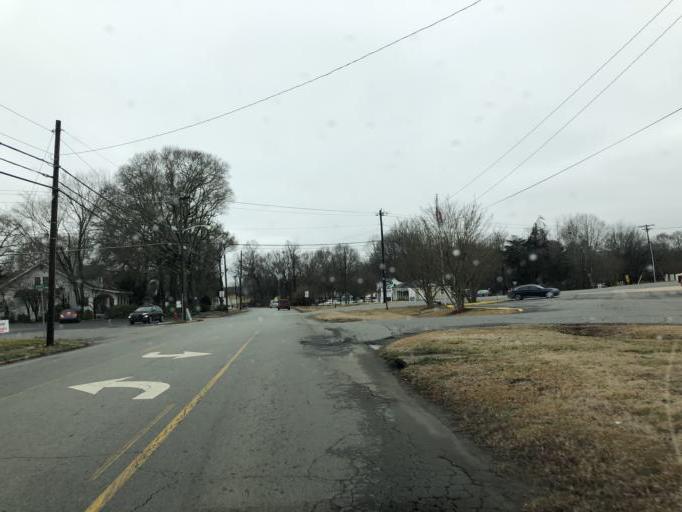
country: US
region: North Carolina
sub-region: Gaston County
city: Ranlo
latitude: 35.2867
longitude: -81.1301
